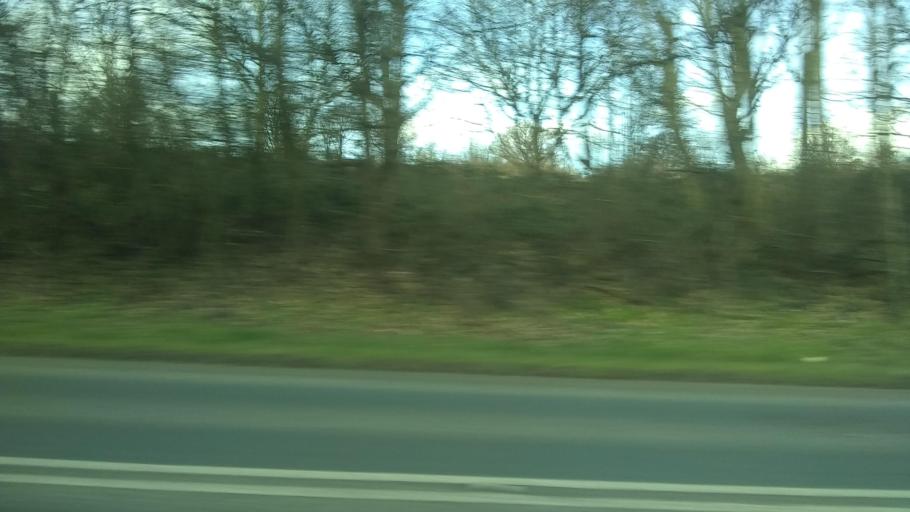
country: GB
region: England
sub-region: Worcestershire
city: Bewdley
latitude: 52.3687
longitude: -2.3315
